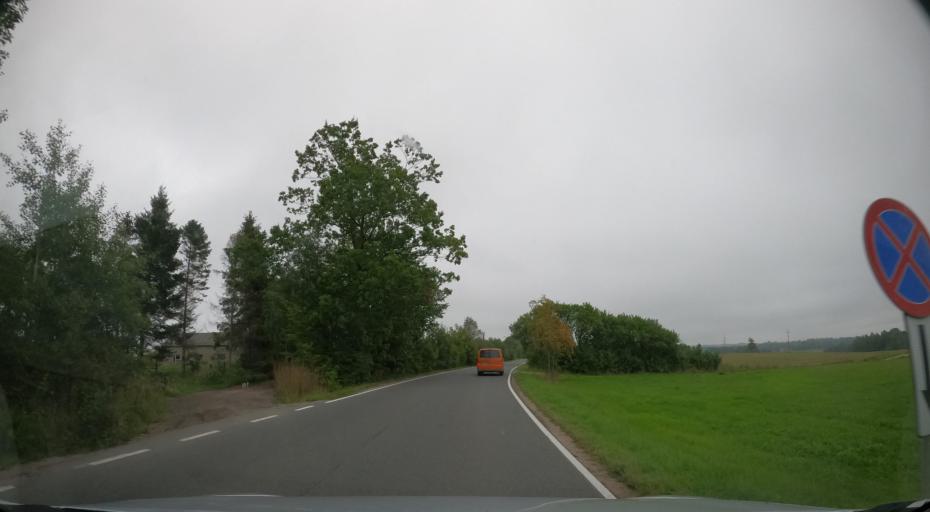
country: PL
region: Pomeranian Voivodeship
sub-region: Powiat wejherowski
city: Szemud
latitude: 54.4999
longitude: 18.1773
